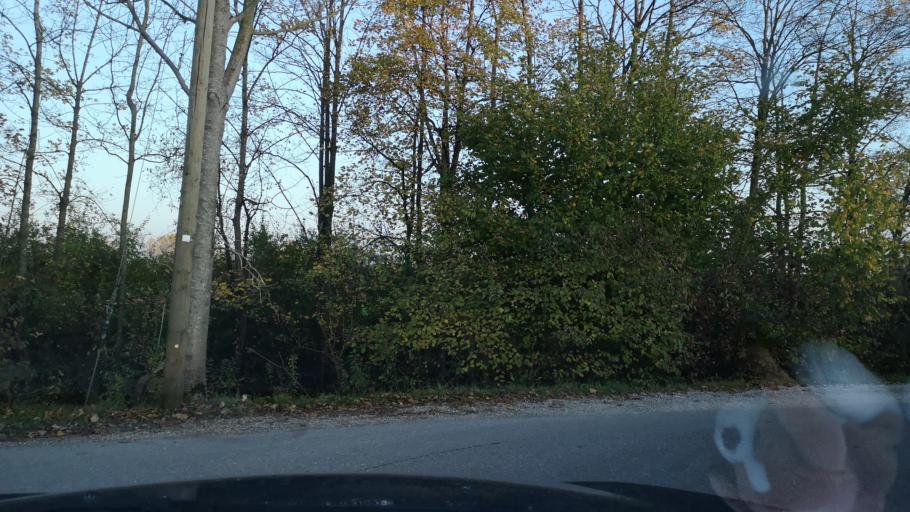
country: DE
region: Bavaria
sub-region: Upper Bavaria
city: Eichenried
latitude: 48.2472
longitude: 11.7521
